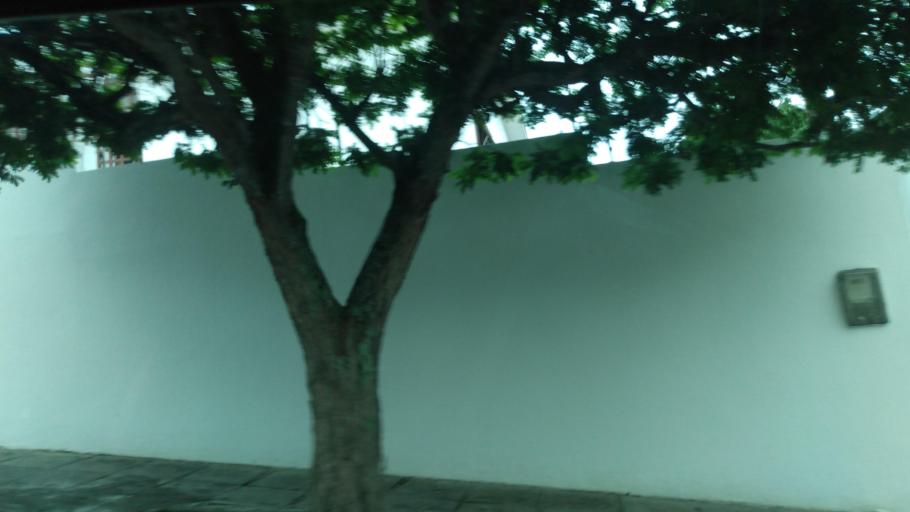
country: BR
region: Pernambuco
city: Garanhuns
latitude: -8.8909
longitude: -36.4891
